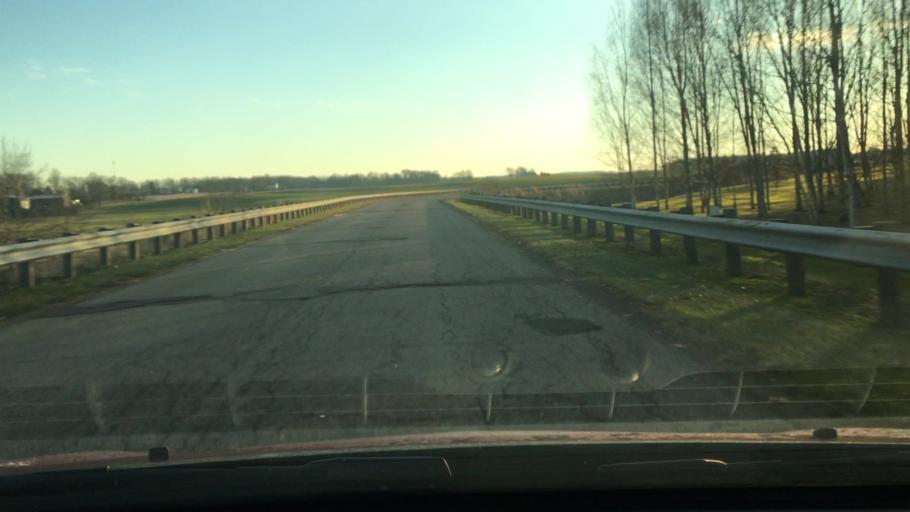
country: US
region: Ohio
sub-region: Wayne County
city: Wooster
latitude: 40.7759
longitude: -81.9133
